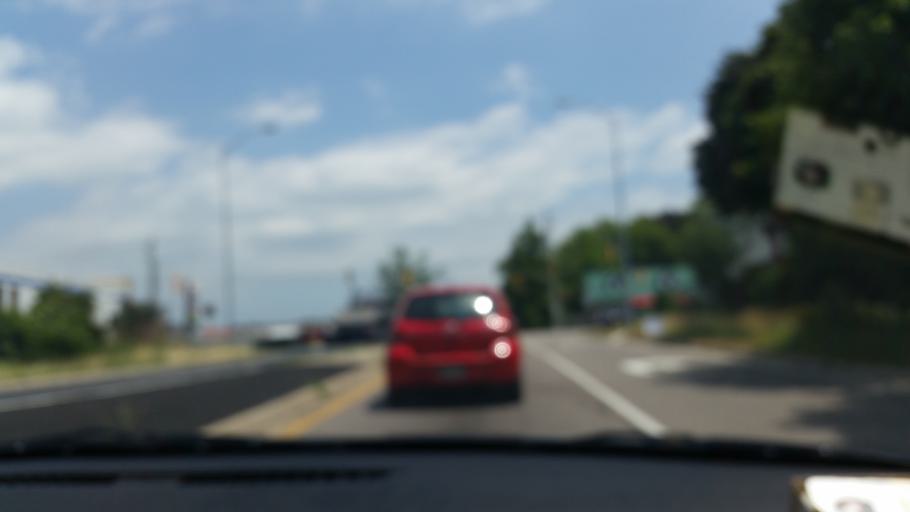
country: CA
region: Ontario
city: Waterloo
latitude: 43.4612
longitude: -80.4697
